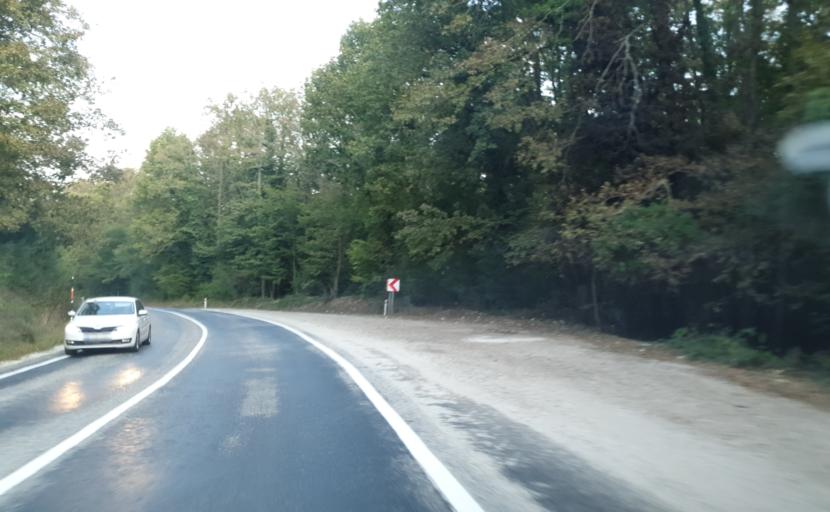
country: TR
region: Kirklareli
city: Igneada
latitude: 41.8799
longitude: 27.9017
